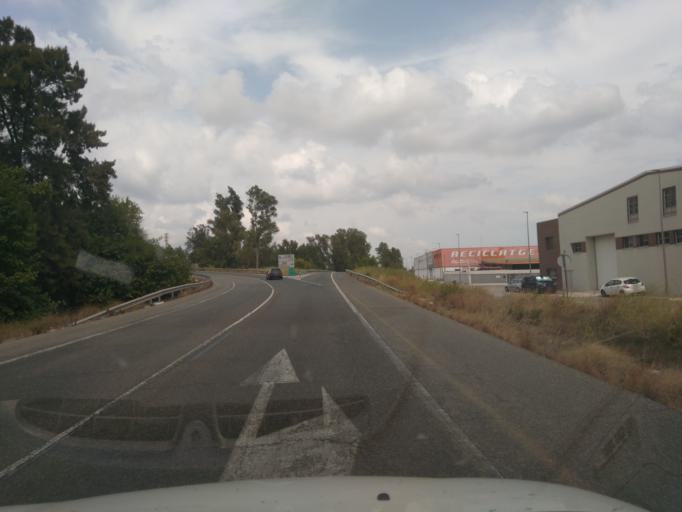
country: ES
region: Valencia
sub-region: Provincia de Valencia
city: Alzira
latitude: 39.1585
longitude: -0.4485
